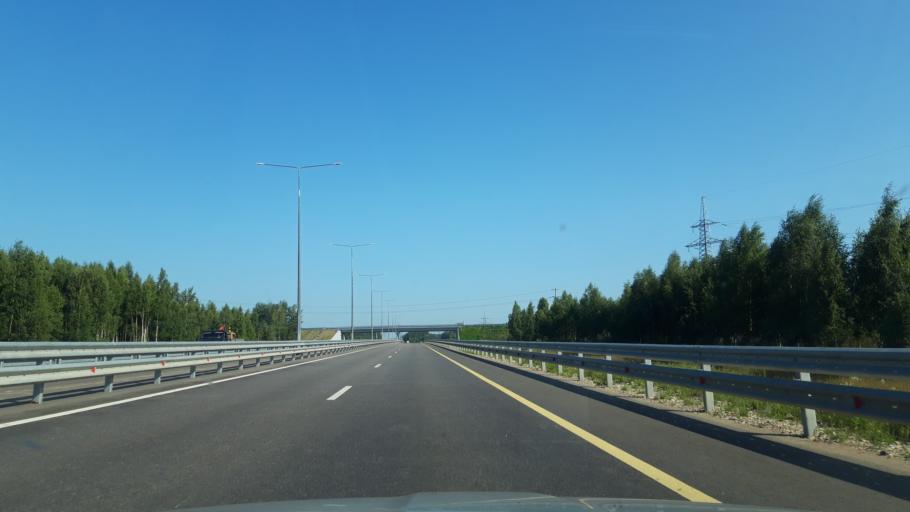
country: RU
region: Tverskaya
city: Zavidovo
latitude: 56.5446
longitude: 36.4915
